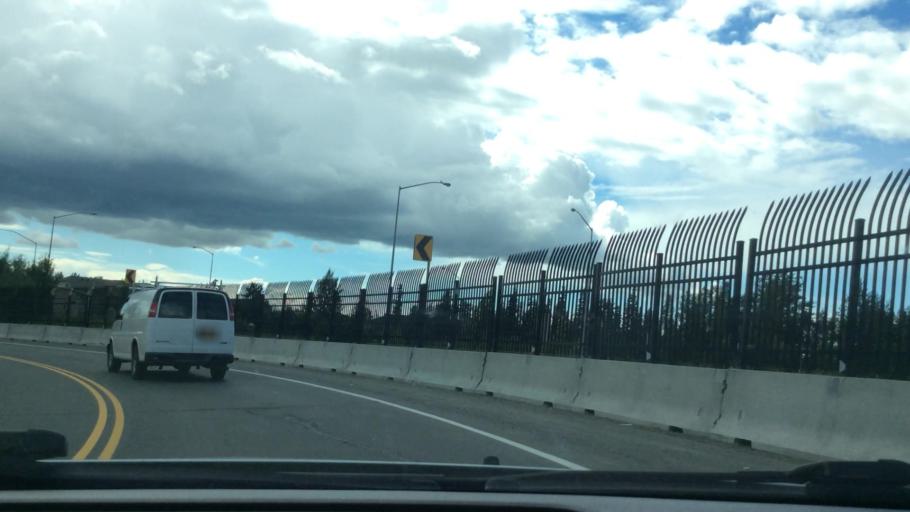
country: US
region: Alaska
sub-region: Anchorage Municipality
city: Elmendorf Air Force Base
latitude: 61.2240
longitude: -149.7547
